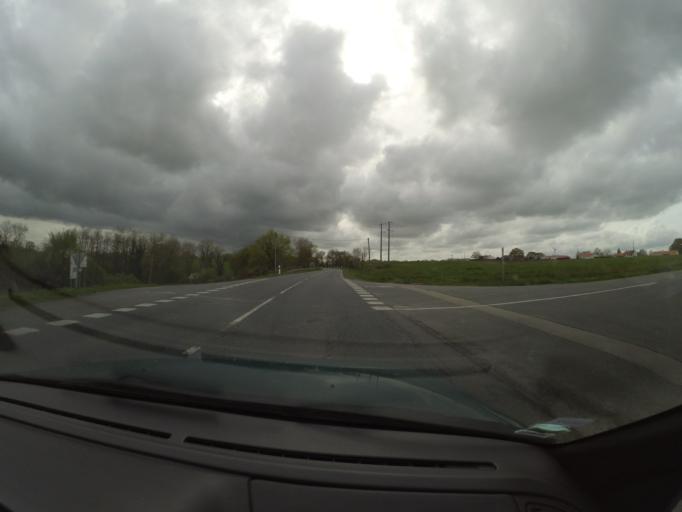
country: FR
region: Pays de la Loire
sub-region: Departement de la Loire-Atlantique
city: La Remaudiere
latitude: 47.2257
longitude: -1.2290
